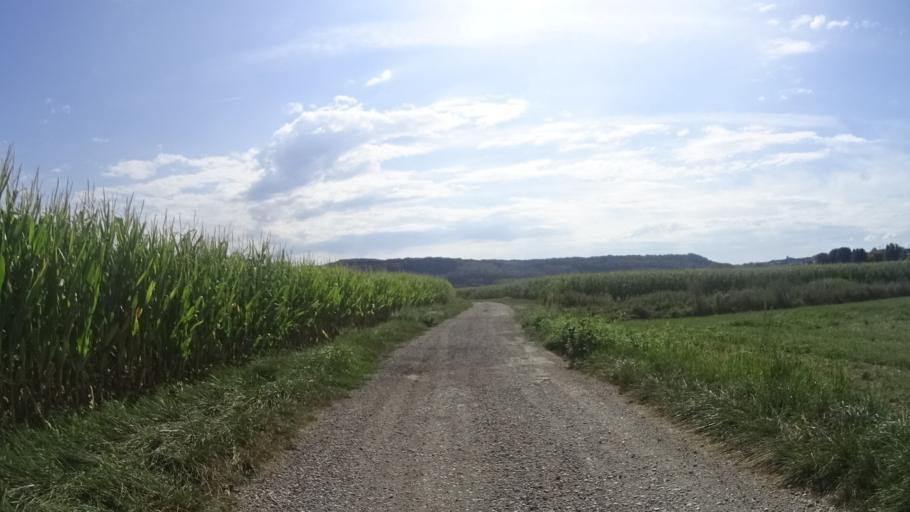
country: FR
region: Franche-Comte
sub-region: Departement du Doubs
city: Thise
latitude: 47.2660
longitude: 6.0810
